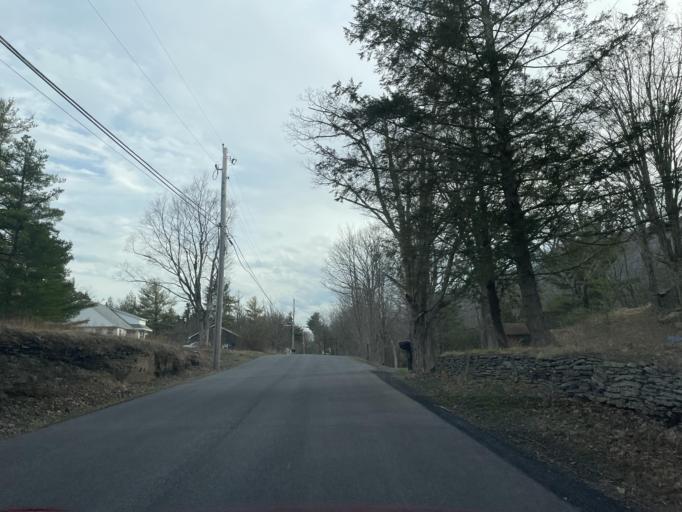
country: US
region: New York
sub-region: Ulster County
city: Manorville
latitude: 42.1570
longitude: -74.0296
